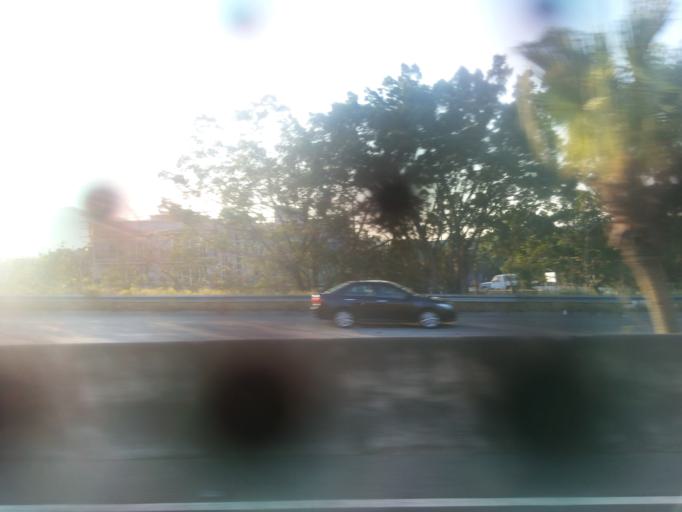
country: HK
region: Yuen Long
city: Yuen Long Kau Hui
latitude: 22.4418
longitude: 113.9988
